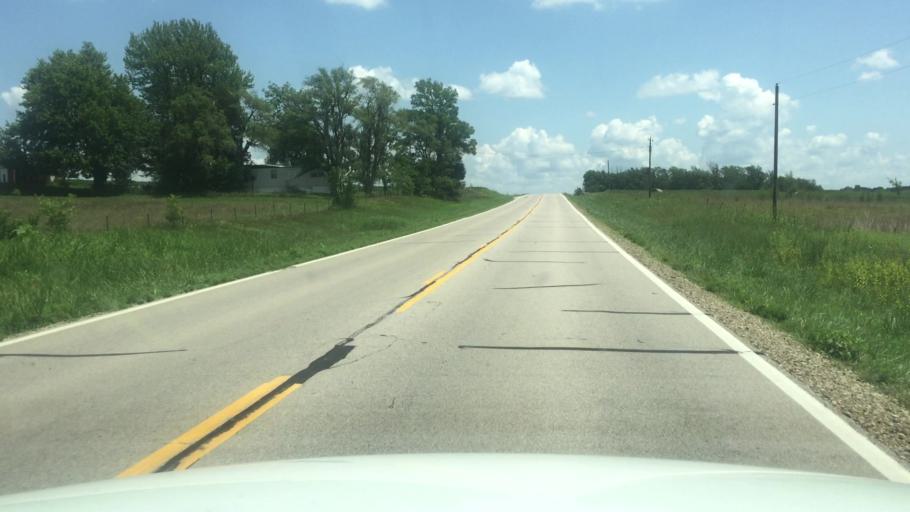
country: US
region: Kansas
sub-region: Brown County
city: Horton
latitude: 39.6674
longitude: -95.5705
